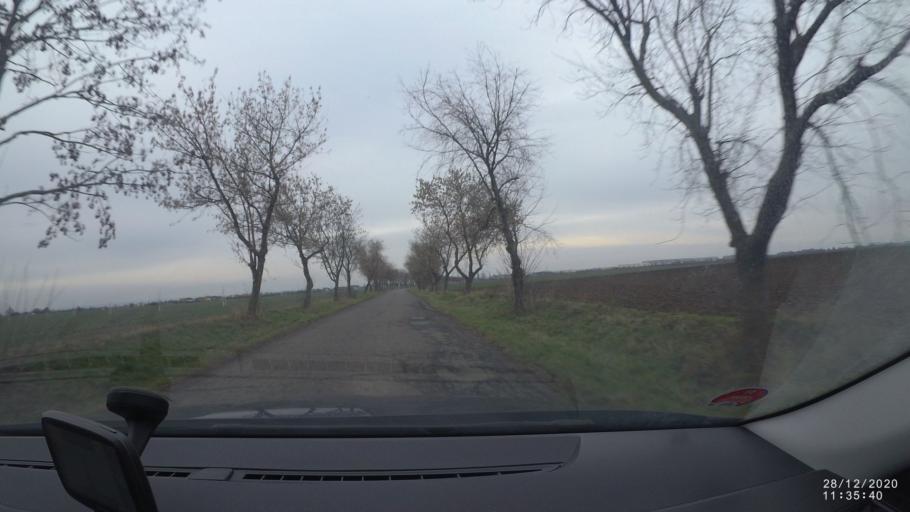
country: CZ
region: Praha
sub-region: Praha 20
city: Horni Pocernice
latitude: 50.1347
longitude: 14.6001
